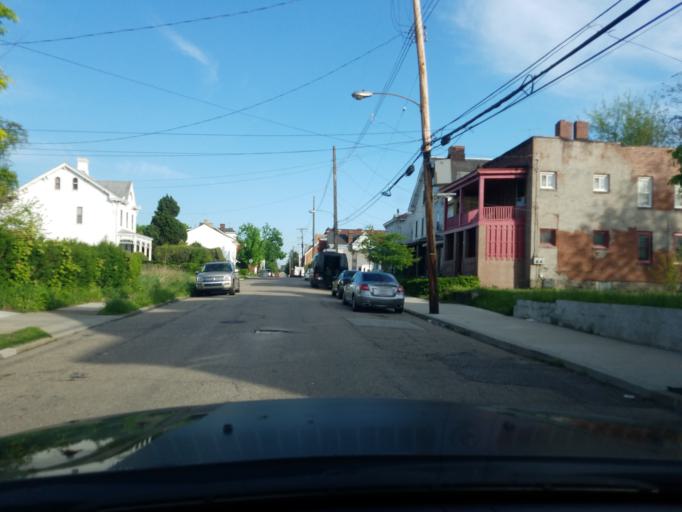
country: US
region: Pennsylvania
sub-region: Allegheny County
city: Aspinwall
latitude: 40.4639
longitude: -79.9156
